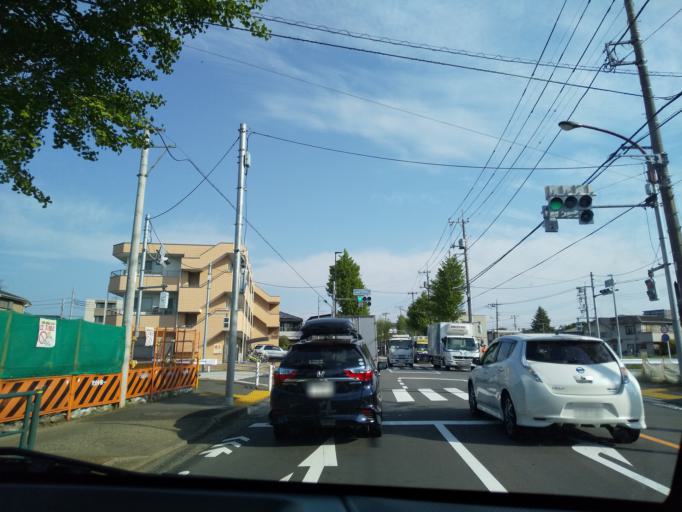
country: JP
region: Tokyo
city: Hino
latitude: 35.6529
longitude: 139.3800
